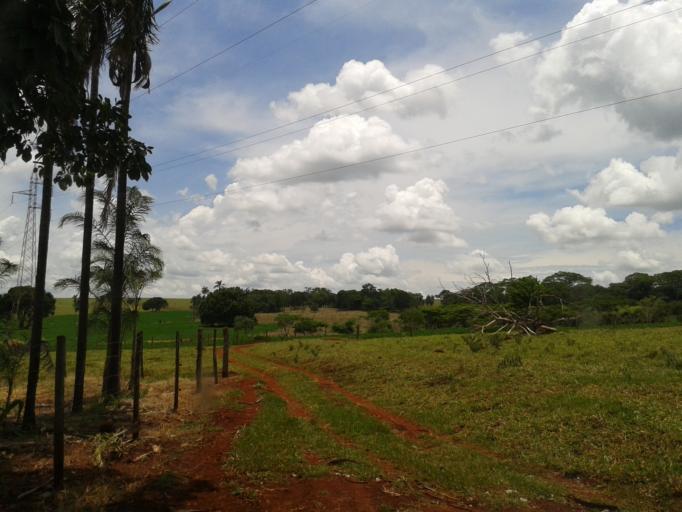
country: BR
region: Minas Gerais
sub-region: Centralina
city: Centralina
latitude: -18.7002
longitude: -49.2294
